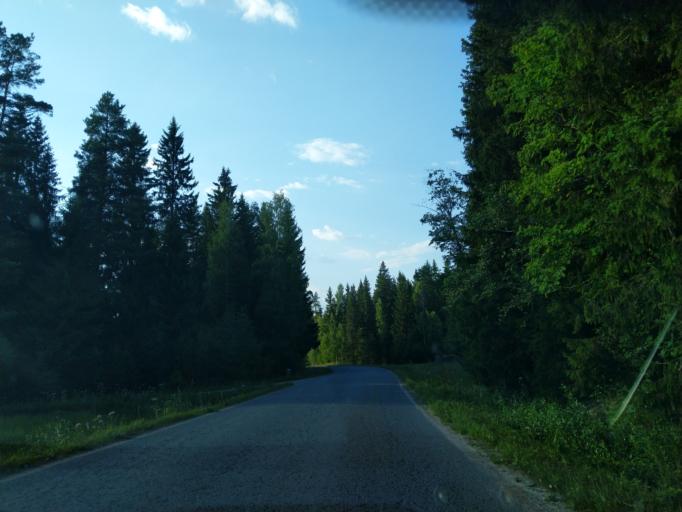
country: FI
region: Satakunta
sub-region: Pori
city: Laengelmaeki
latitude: 61.8016
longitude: 22.1950
